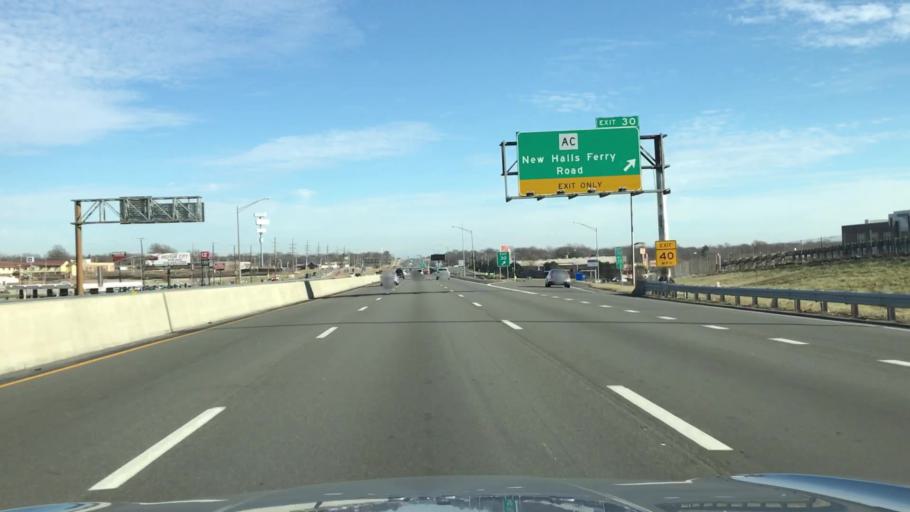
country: US
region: Missouri
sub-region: Saint Louis County
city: Black Jack
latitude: 38.7710
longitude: -90.2701
